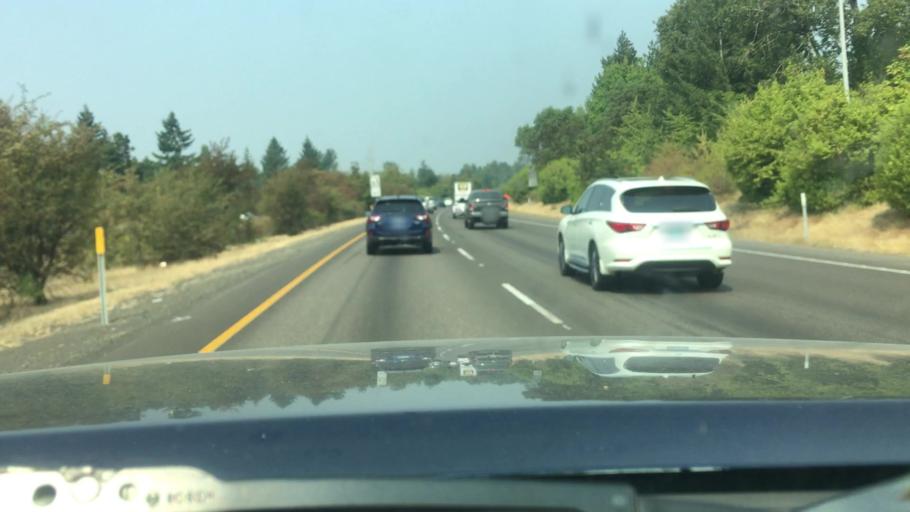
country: US
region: Oregon
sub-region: Clackamas County
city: West Linn
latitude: 45.3495
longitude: -122.6574
